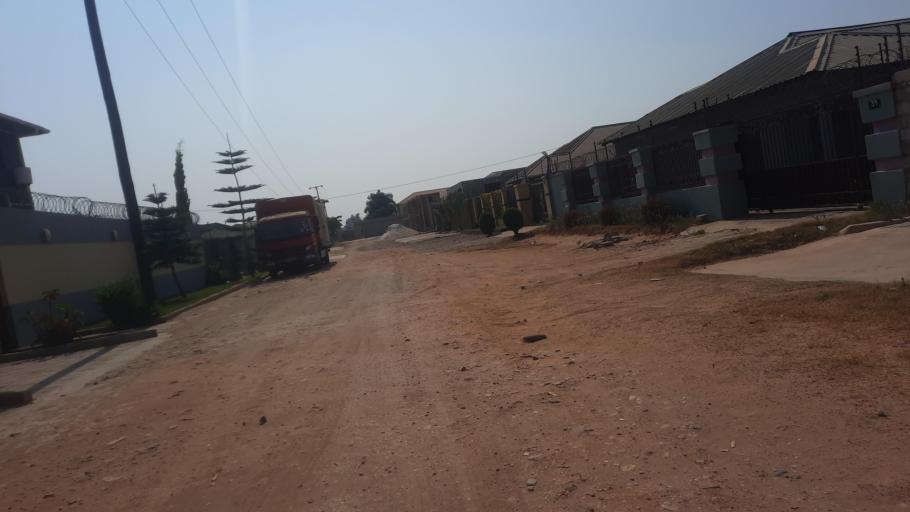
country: ZM
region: Lusaka
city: Lusaka
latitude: -15.3942
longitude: 28.3862
